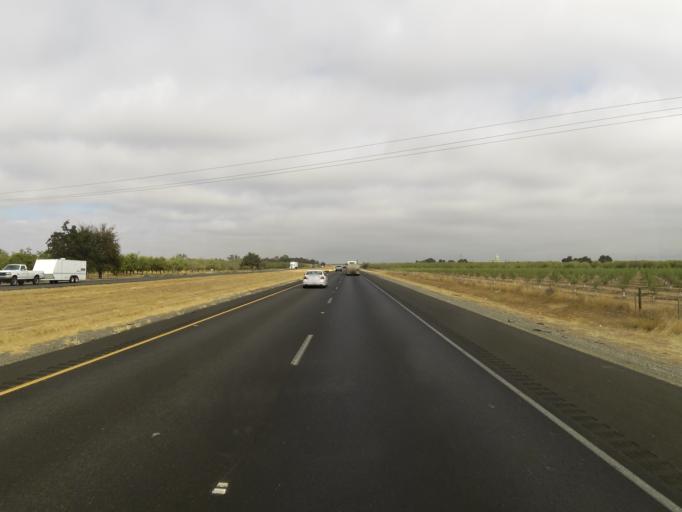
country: US
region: California
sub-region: Yolo County
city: Dunnigan
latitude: 38.9153
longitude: -121.9933
